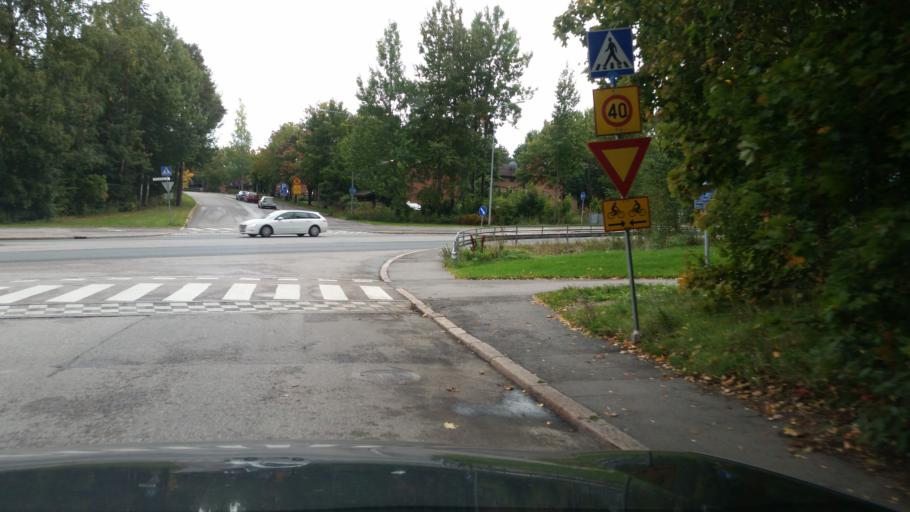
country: FI
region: Uusimaa
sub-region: Helsinki
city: Helsinki
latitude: 60.2361
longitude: 24.9713
